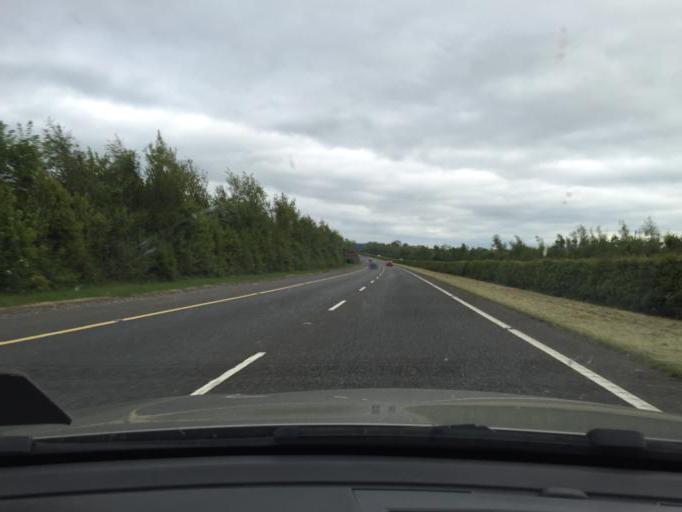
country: IE
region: Leinster
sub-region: An Mhi
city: Stamullin
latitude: 53.6156
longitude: -6.2425
